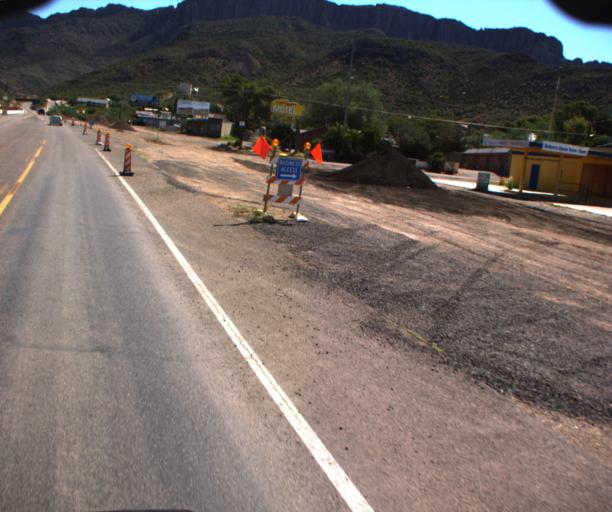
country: US
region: Arizona
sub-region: Pinal County
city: Superior
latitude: 33.2882
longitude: -111.1024
